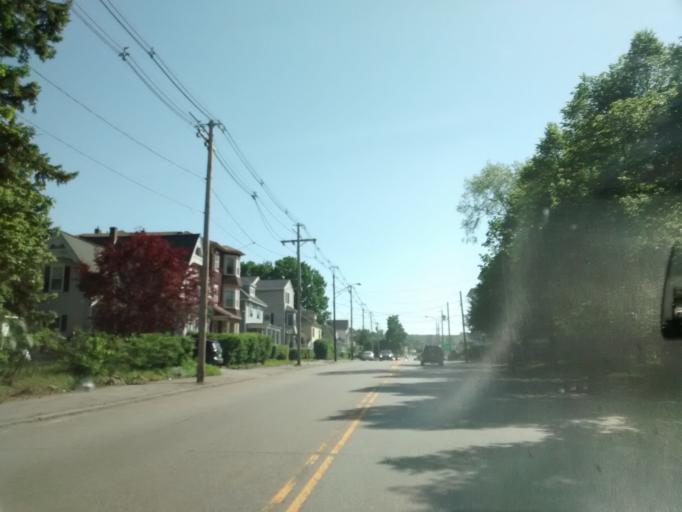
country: US
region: Massachusetts
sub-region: Worcester County
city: Worcester
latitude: 42.2429
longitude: -71.8389
